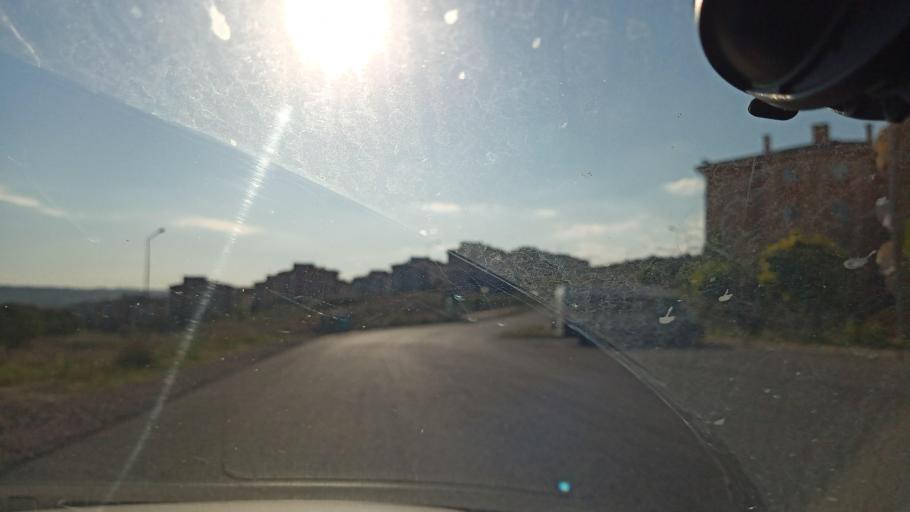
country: TR
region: Kocaeli
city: Kaymaz
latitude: 40.8605
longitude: 30.2793
